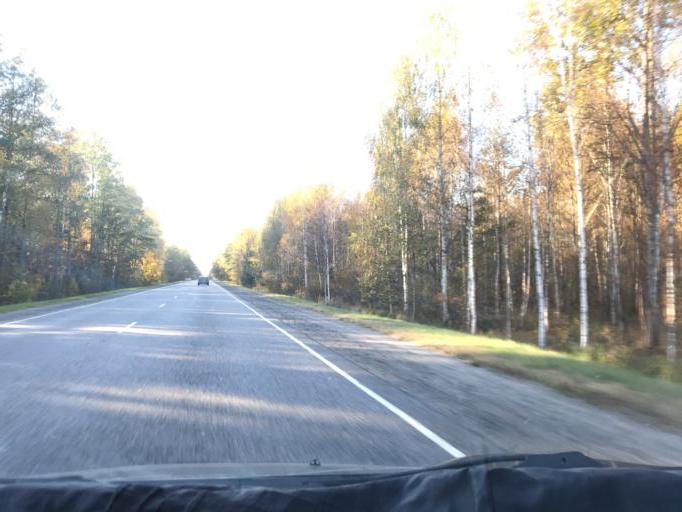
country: BY
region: Gomel
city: Pyetrykaw
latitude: 52.2596
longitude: 28.3334
